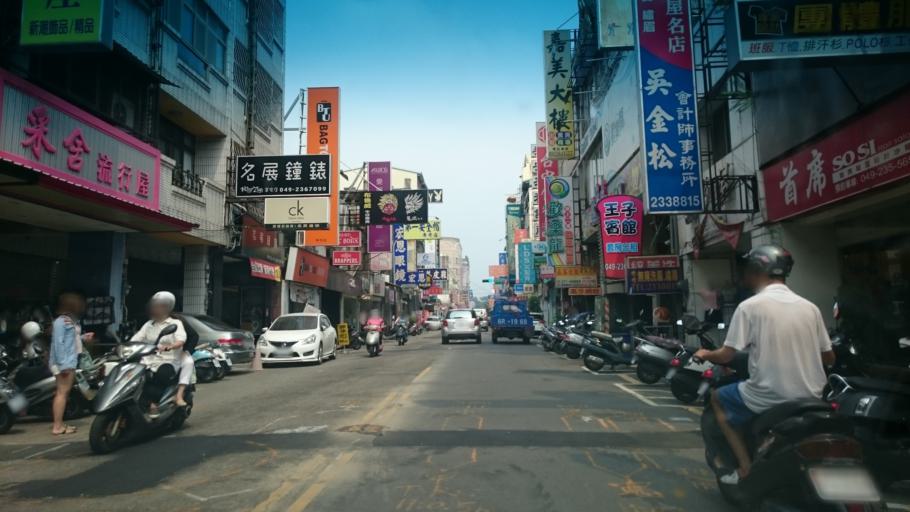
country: TW
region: Taiwan
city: Zhongxing New Village
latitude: 23.9780
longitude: 120.6830
